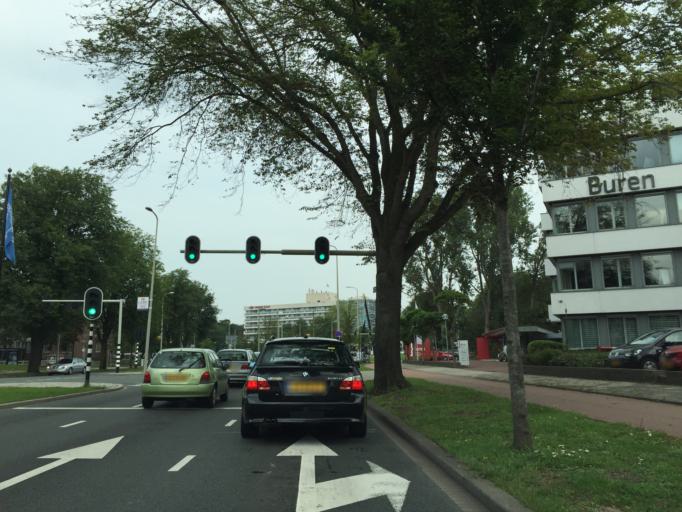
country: NL
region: South Holland
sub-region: Gemeente Den Haag
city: Scheveningen
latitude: 52.0947
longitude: 4.2856
